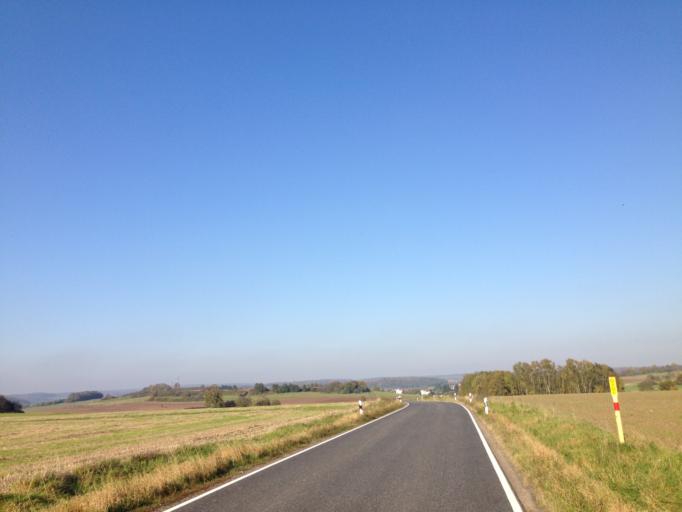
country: DE
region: Hesse
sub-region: Regierungsbezirk Giessen
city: Reiskirchen
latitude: 50.5655
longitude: 8.8094
